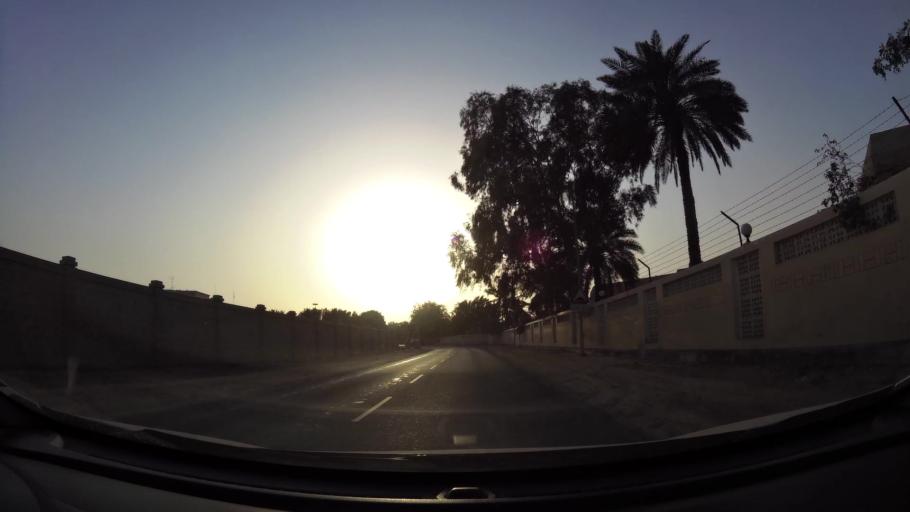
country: BH
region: Manama
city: Jidd Hafs
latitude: 26.2018
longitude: 50.4915
